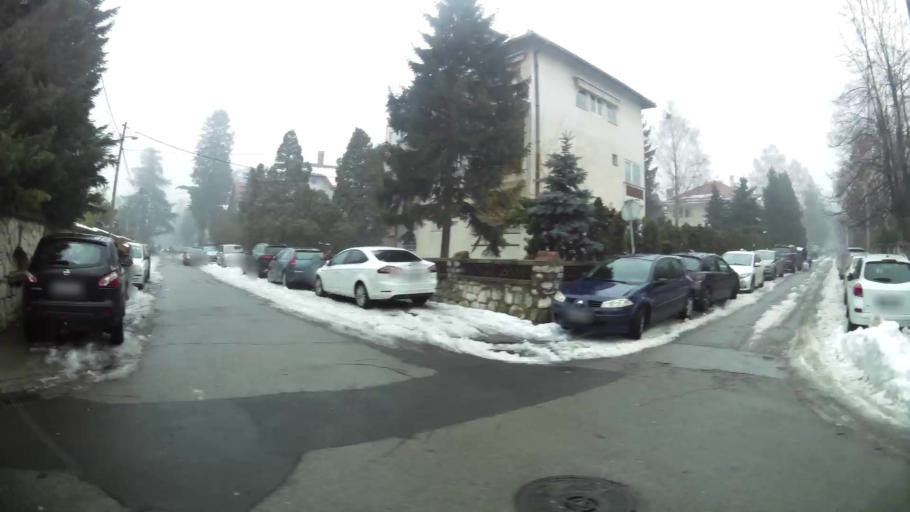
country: RS
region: Central Serbia
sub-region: Belgrade
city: Savski Venac
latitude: 44.7734
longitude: 20.4646
